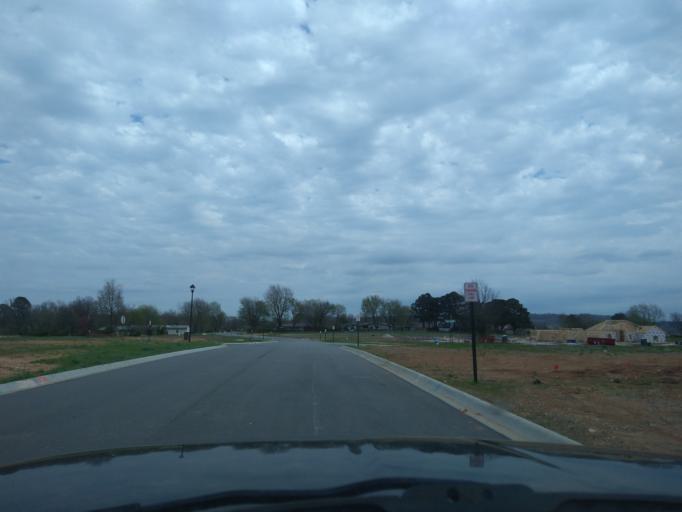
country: US
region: Arkansas
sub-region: Washington County
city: Farmington
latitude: 36.0710
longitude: -94.2437
